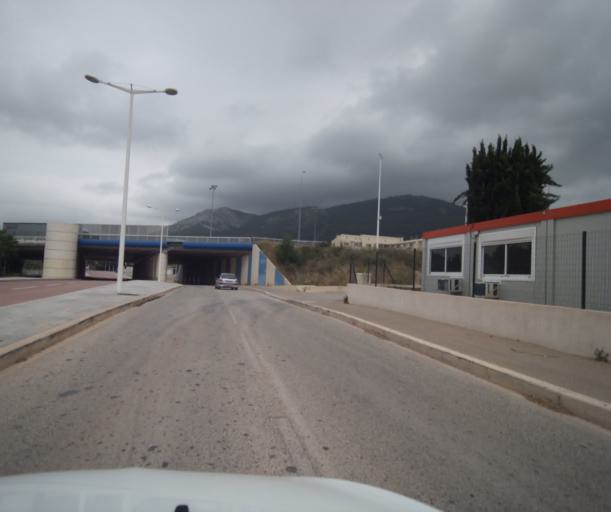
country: FR
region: Provence-Alpes-Cote d'Azur
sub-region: Departement du Var
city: La Valette-du-Var
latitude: 43.1251
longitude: 5.9724
